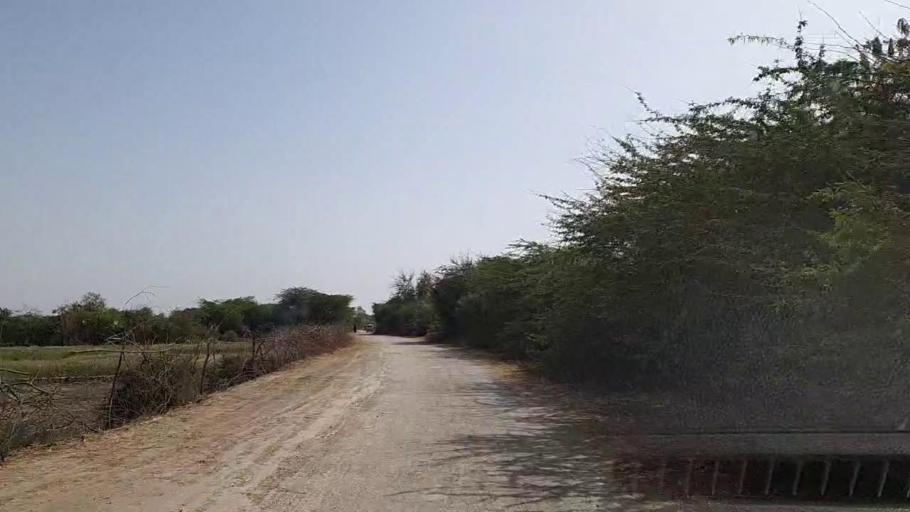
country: PK
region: Sindh
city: Jati
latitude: 24.3601
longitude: 68.2734
